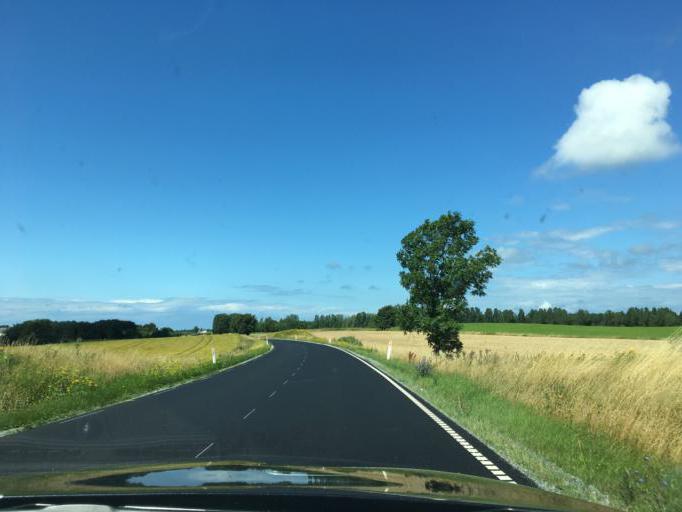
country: DK
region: Capital Region
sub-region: Gribskov Kommune
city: Helsinge
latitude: 56.0739
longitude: 12.1973
